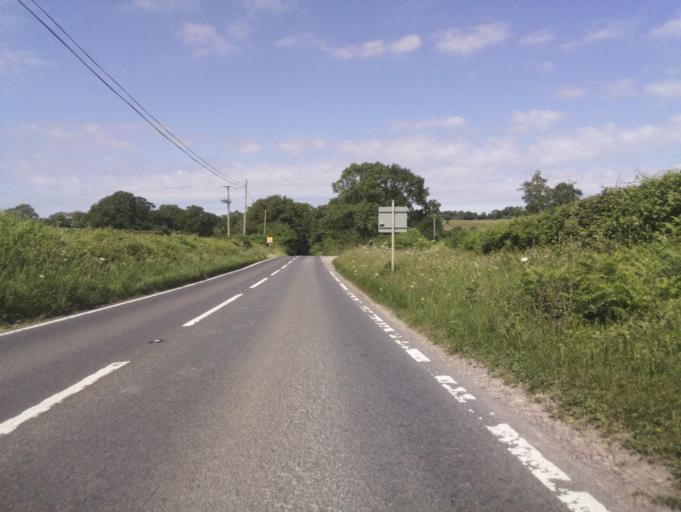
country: GB
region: England
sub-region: Somerset
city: Redlynch
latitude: 51.0608
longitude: -2.4580
